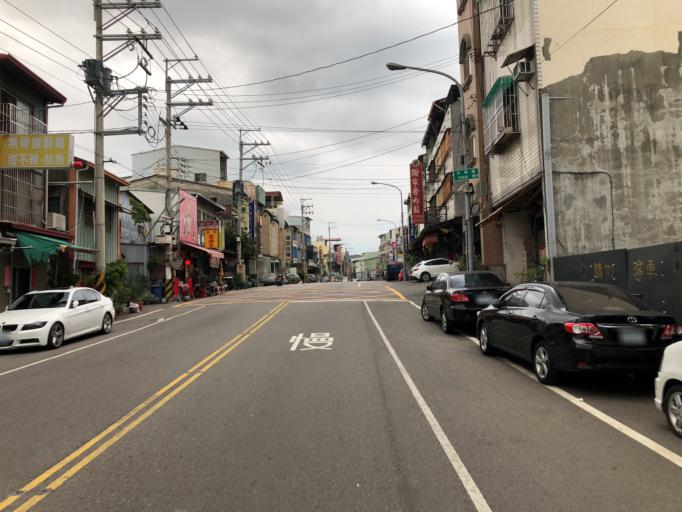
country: TW
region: Taiwan
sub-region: Taichung City
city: Taichung
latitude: 24.1198
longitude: 120.7337
